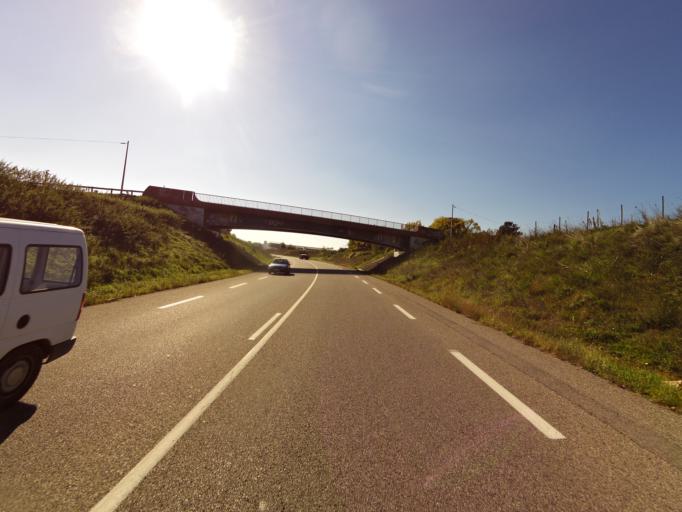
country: FR
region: Rhone-Alpes
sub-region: Departement de l'Ardeche
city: Saint-Privat
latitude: 44.6189
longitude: 4.4106
